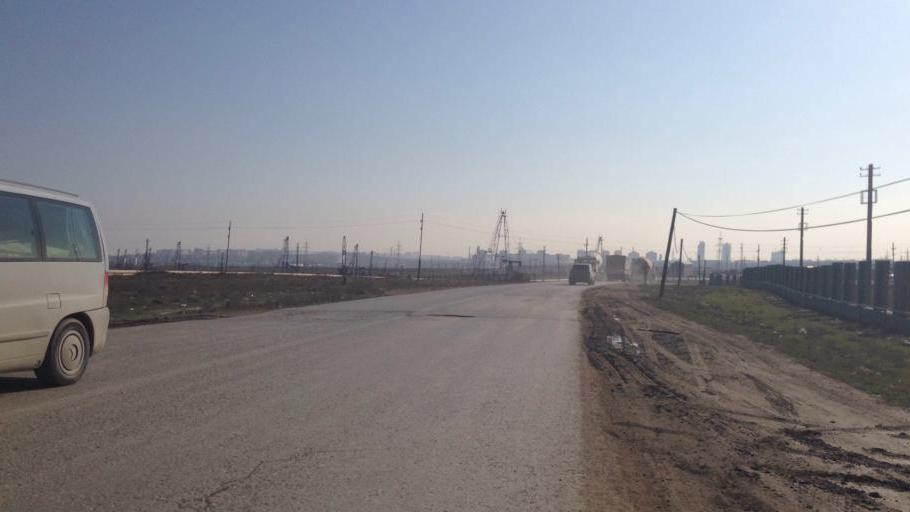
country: AZ
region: Baki
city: Balakhani
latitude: 40.4591
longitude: 49.8910
